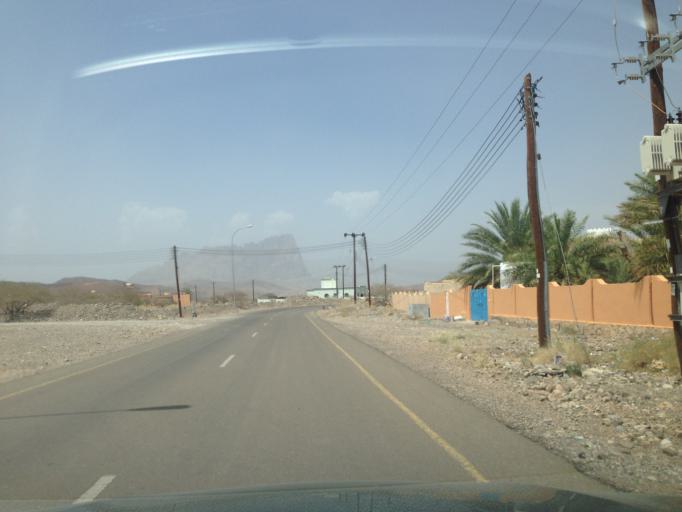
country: OM
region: Az Zahirah
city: `Ibri
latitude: 23.1737
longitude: 56.9078
